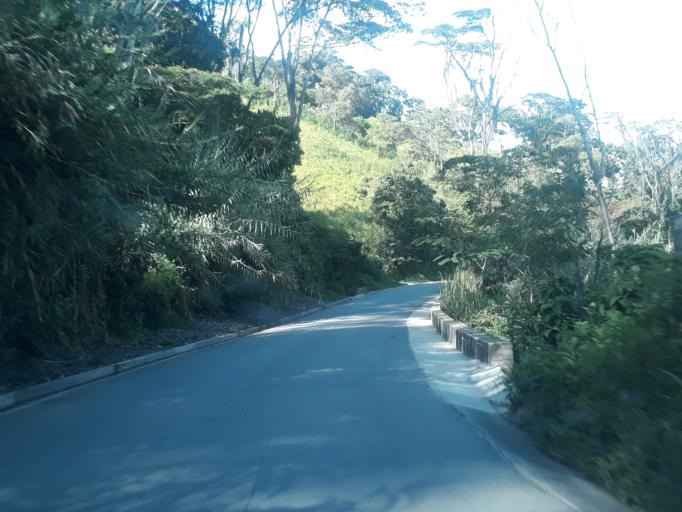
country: CO
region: Santander
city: Velez
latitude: 6.0329
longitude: -73.6550
